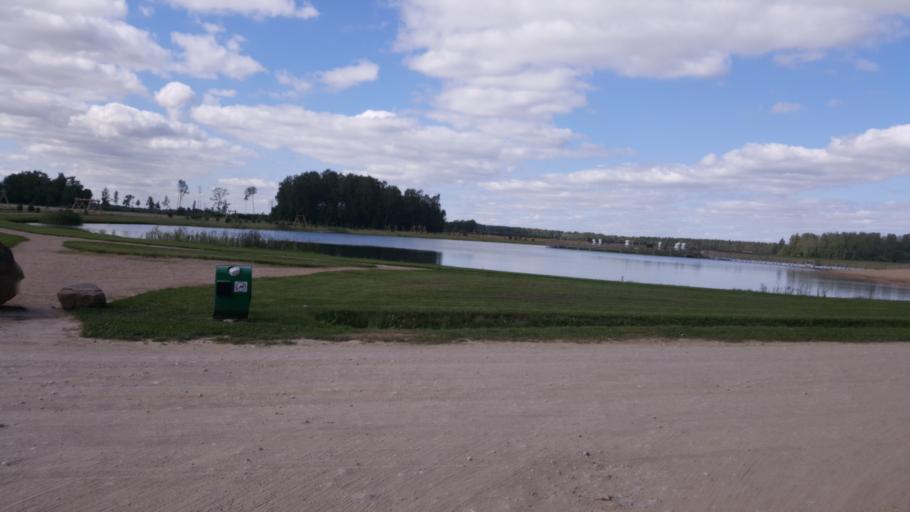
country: LT
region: Siauliu apskritis
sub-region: Siauliai
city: Siauliai
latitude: 56.0203
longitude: 23.5019
